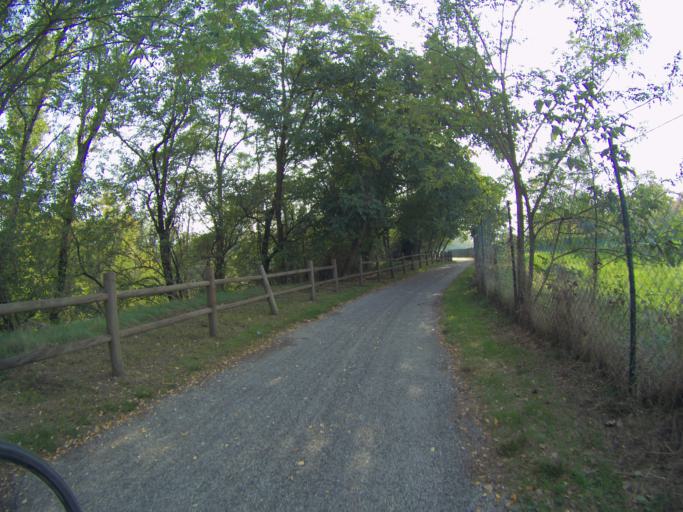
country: IT
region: Emilia-Romagna
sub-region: Provincia di Reggio Emilia
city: Albinea
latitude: 44.6606
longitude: 10.6019
